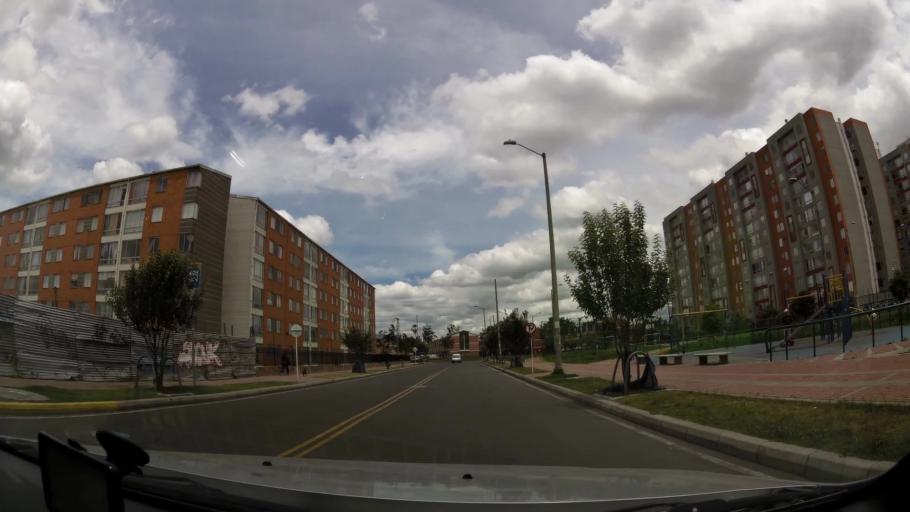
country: CO
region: Cundinamarca
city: Funza
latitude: 4.6539
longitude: -74.1554
